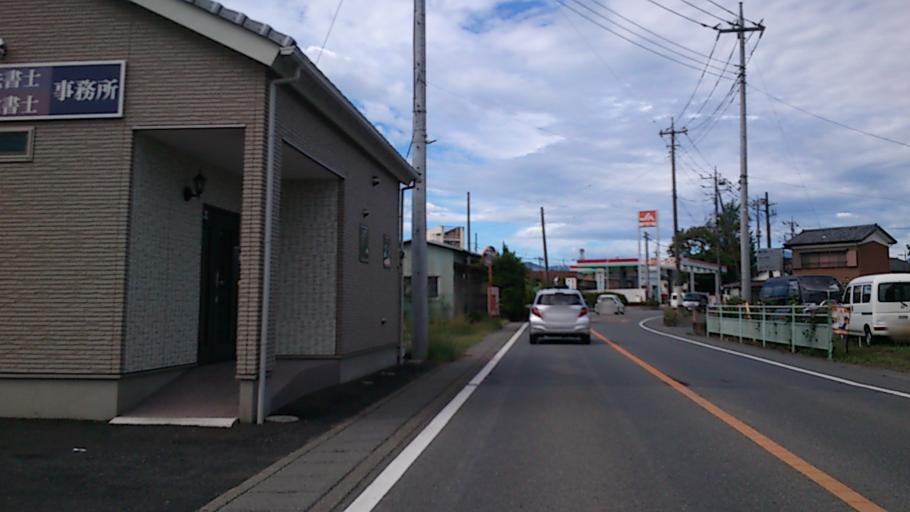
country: JP
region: Gunma
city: Fujioka
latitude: 36.2622
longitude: 139.0941
